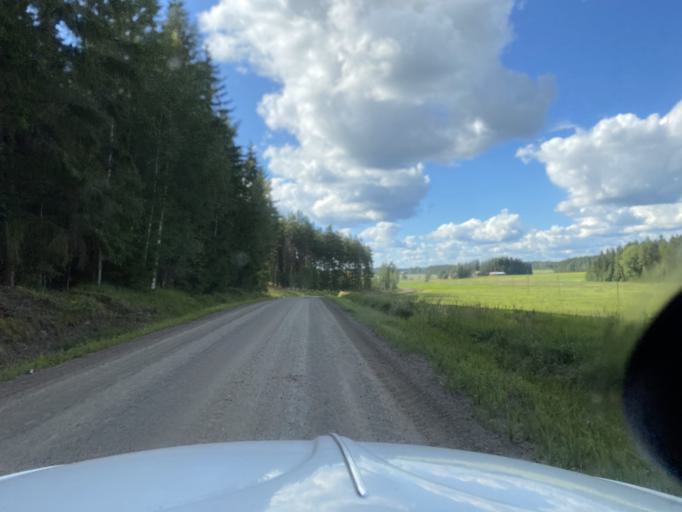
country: FI
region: Pirkanmaa
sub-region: Lounais-Pirkanmaa
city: Punkalaidun
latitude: 61.1241
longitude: 23.2606
